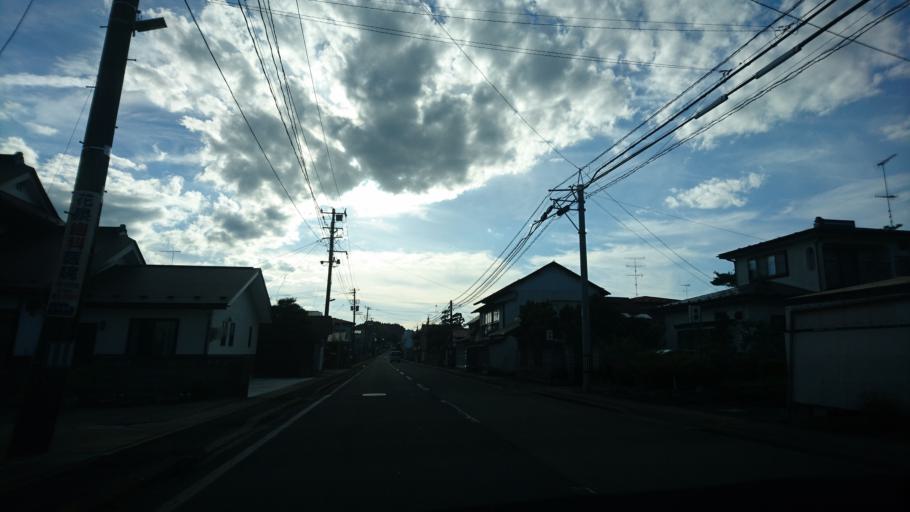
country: JP
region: Iwate
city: Ichinoseki
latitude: 38.8478
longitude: 141.1758
